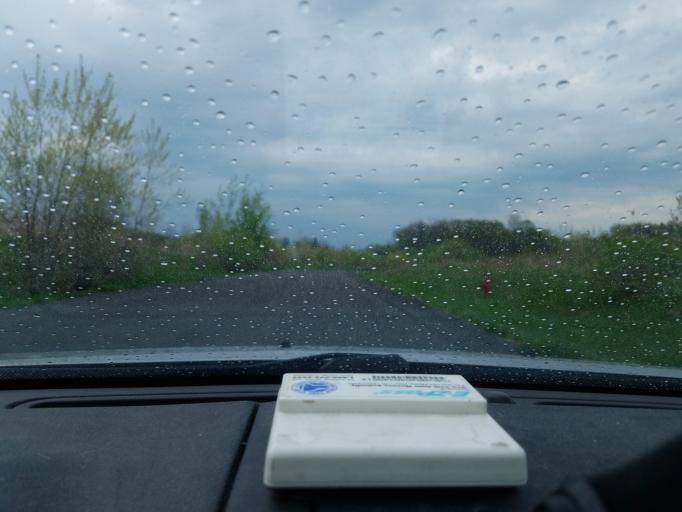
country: US
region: New York
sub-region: Onondaga County
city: East Syracuse
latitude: 43.1069
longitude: -76.0862
